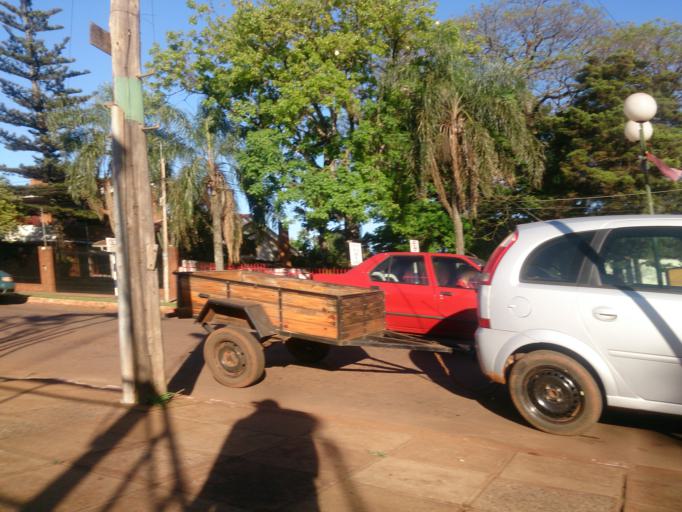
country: AR
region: Misiones
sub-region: Departamento de Obera
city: Obera
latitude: -27.4894
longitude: -55.1096
